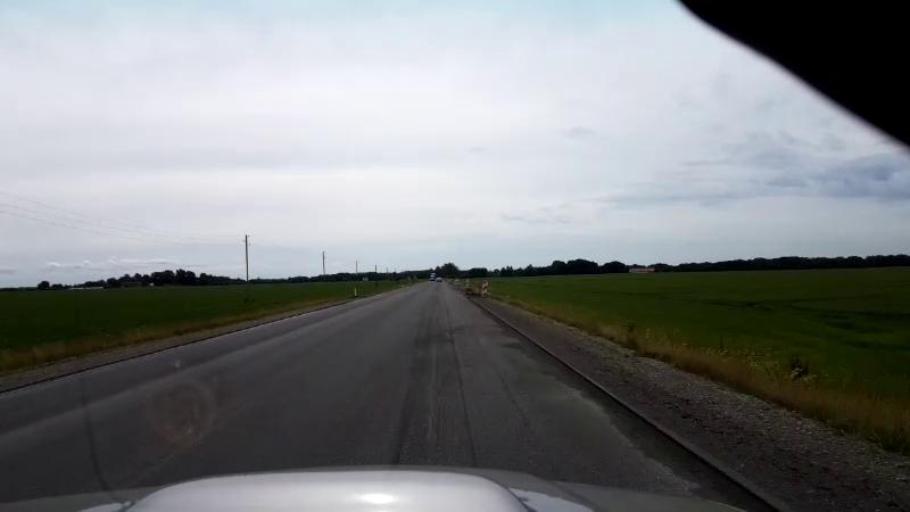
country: LV
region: Bauskas Rajons
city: Bauska
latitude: 56.3373
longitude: 24.2952
